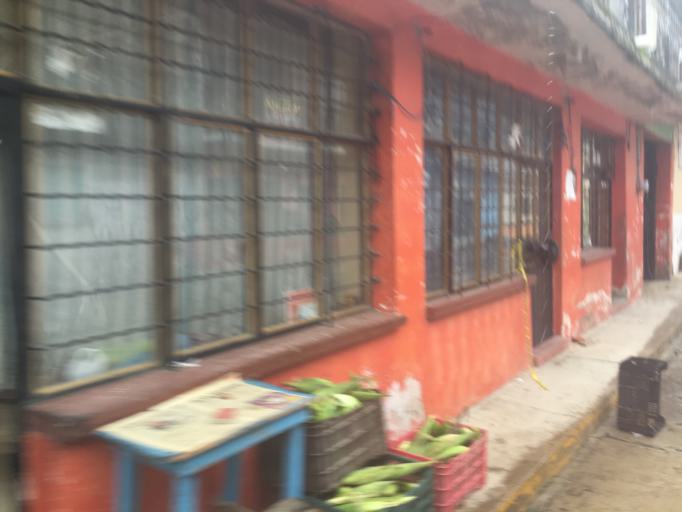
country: MX
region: Morelos
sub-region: Tlayacapan
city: Tlayacapan
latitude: 18.9542
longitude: -98.9835
